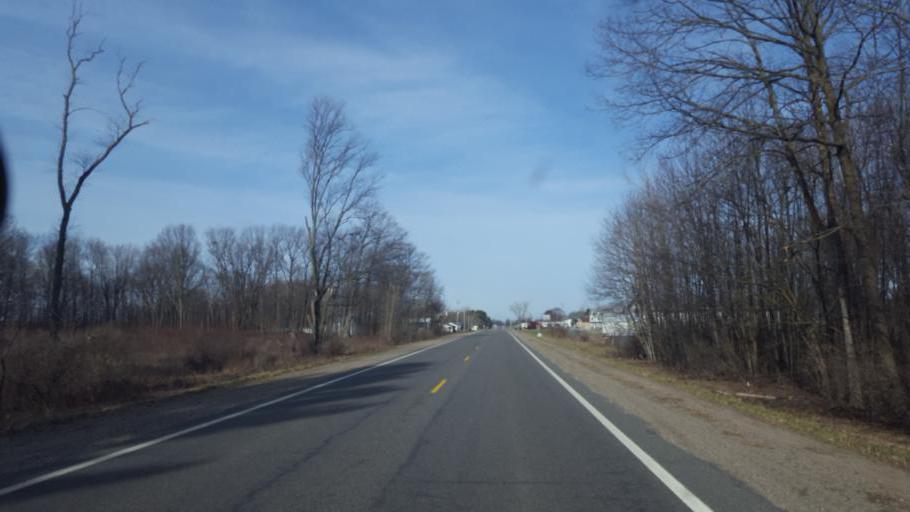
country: US
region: Michigan
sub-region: Montcalm County
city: Lakeview
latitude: 43.4315
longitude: -85.2769
